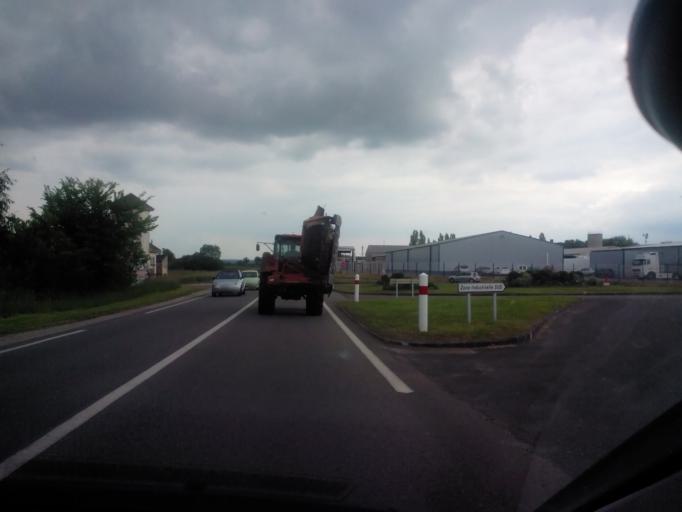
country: FR
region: Lorraine
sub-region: Departement de la Moselle
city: Sarralbe
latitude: 48.9821
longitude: 7.0273
